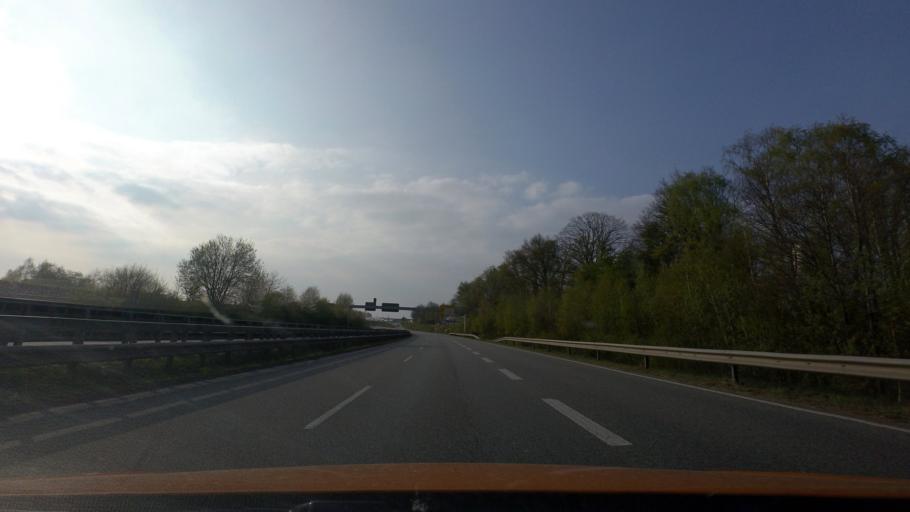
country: DE
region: North Rhine-Westphalia
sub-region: Regierungsbezirk Detmold
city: Herford
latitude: 52.0940
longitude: 8.6883
